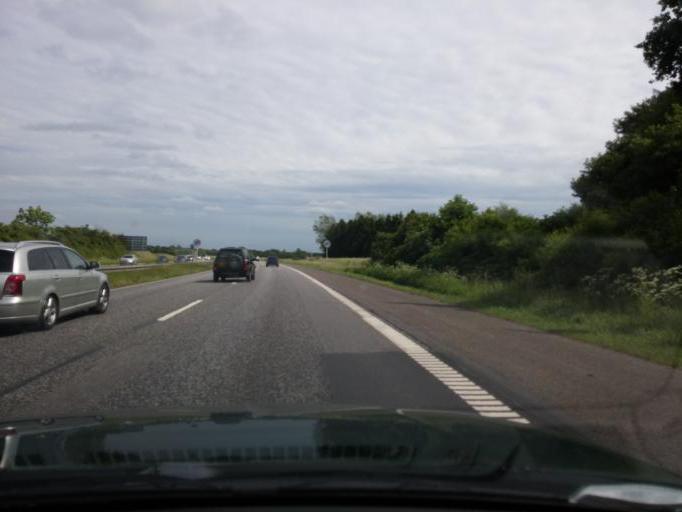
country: DK
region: South Denmark
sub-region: Middelfart Kommune
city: Norre Aby
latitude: 55.4651
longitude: 9.9044
